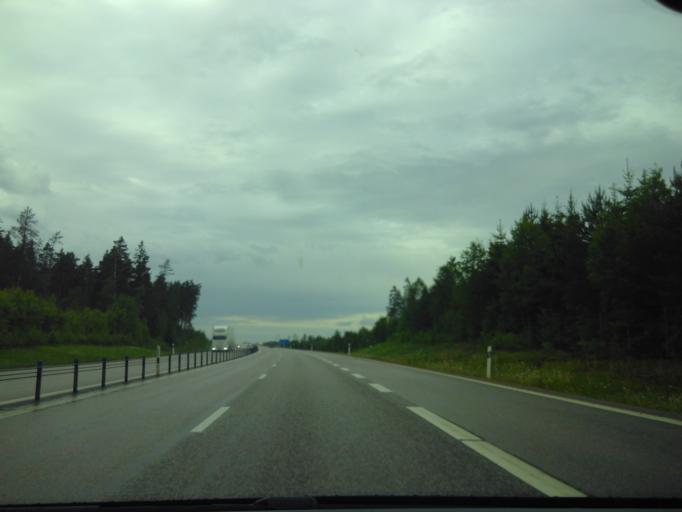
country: SE
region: Vaestra Goetaland
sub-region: Skovde Kommun
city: Skultorp
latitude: 58.3425
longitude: 13.8650
